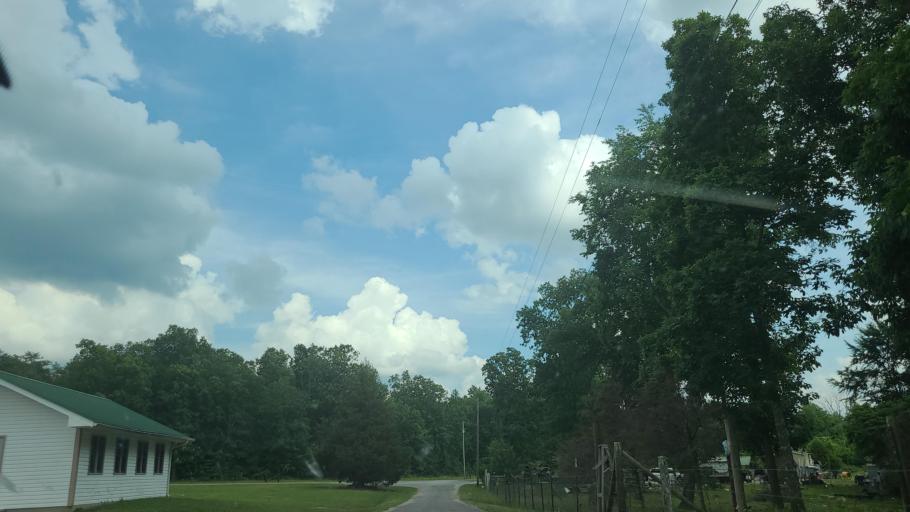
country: US
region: Tennessee
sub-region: Cumberland County
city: Lake Tansi
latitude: 35.7816
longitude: -85.0667
